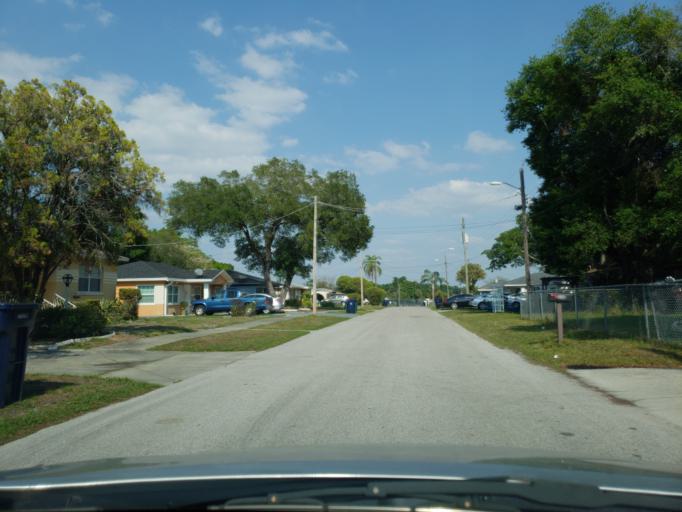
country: US
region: Florida
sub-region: Hillsborough County
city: Tampa
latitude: 27.9645
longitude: -82.4783
